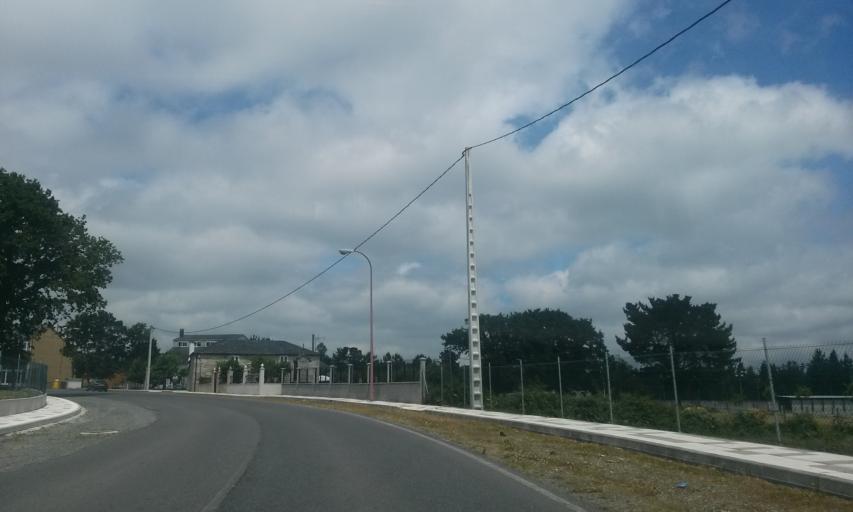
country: ES
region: Galicia
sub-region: Provincia de Lugo
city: Friol
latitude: 43.0344
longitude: -7.7995
